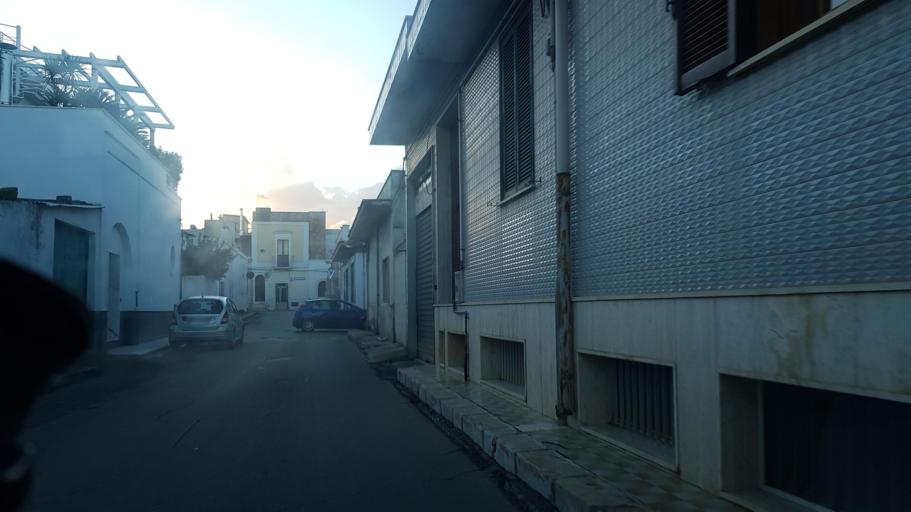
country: IT
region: Apulia
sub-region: Provincia di Brindisi
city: San Michele Salentino
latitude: 40.6319
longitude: 17.6330
